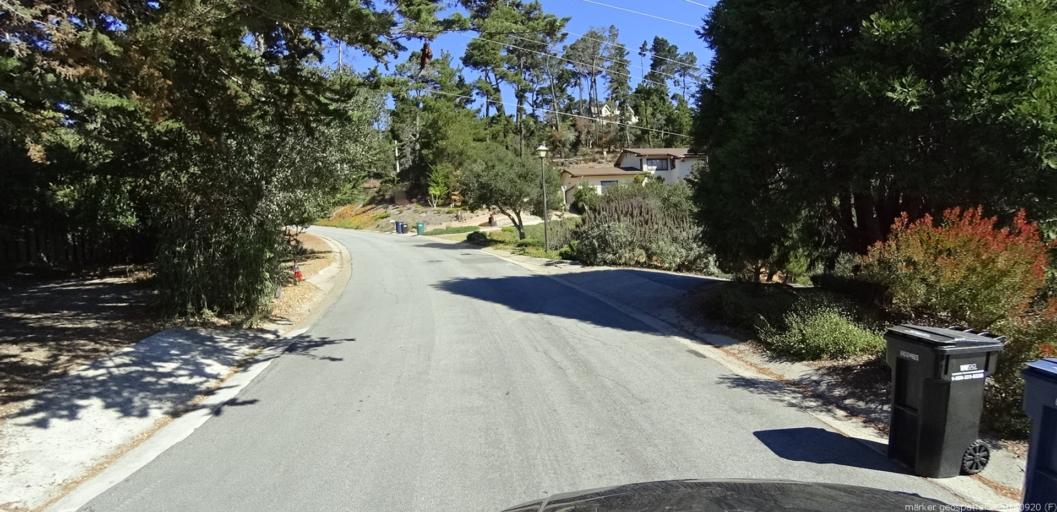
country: US
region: California
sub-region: Monterey County
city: Carmel-by-the-Sea
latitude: 36.5580
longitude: -121.8951
